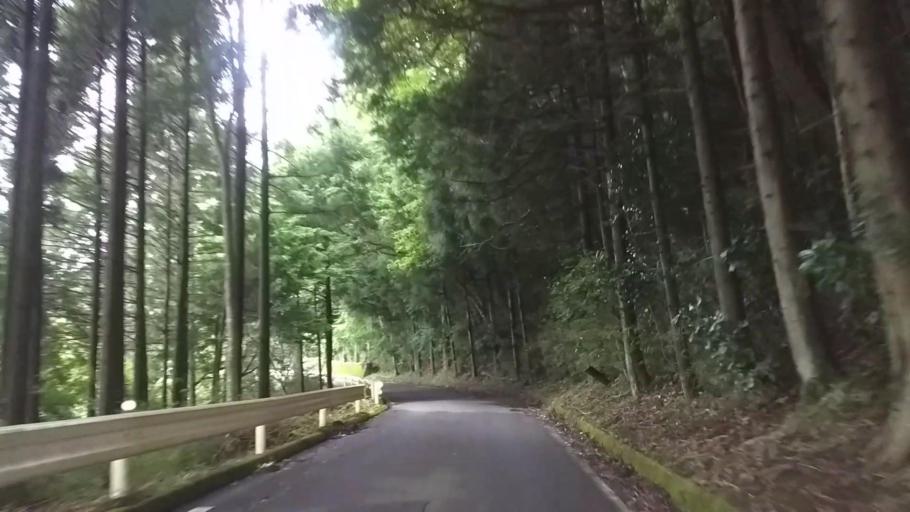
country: JP
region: Shizuoka
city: Gotemba
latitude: 35.3272
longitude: 138.9854
